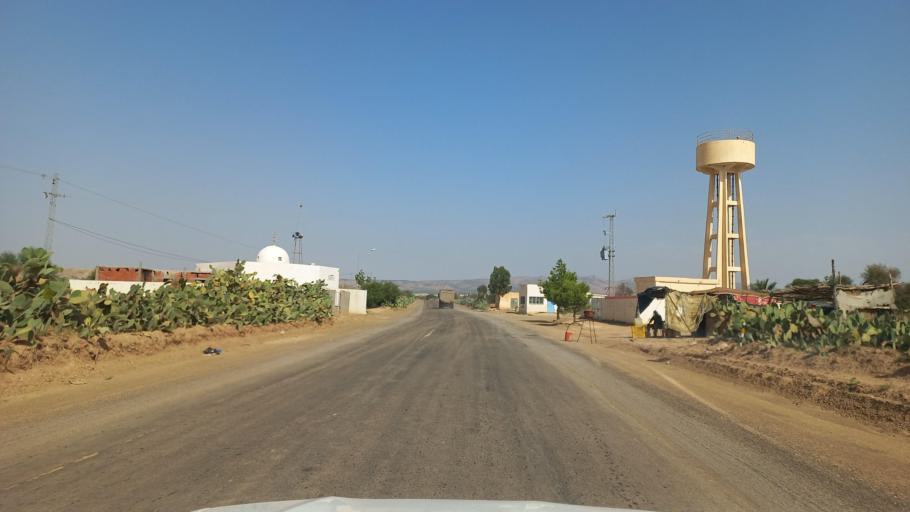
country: TN
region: Al Qasrayn
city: Sbiba
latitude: 35.3534
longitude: 9.0502
